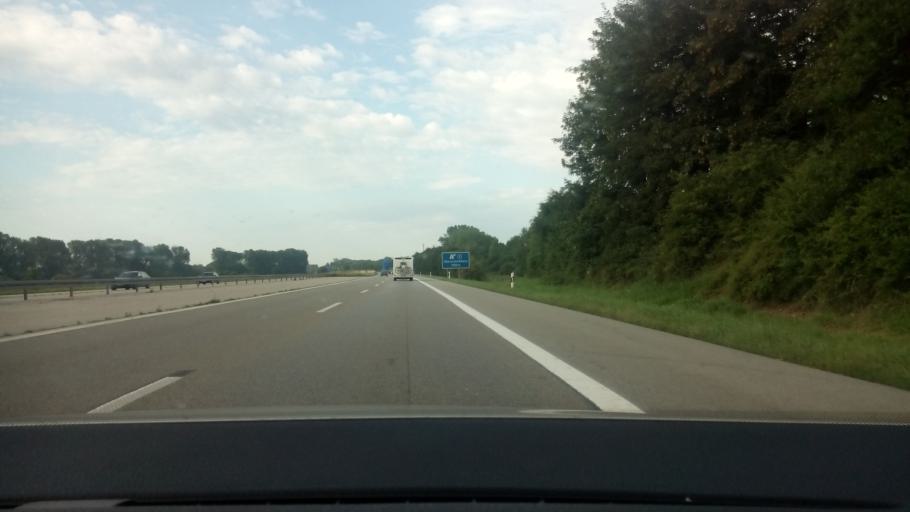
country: DE
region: Bavaria
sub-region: Upper Bavaria
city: Oberschleissheim
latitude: 48.2636
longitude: 11.5366
